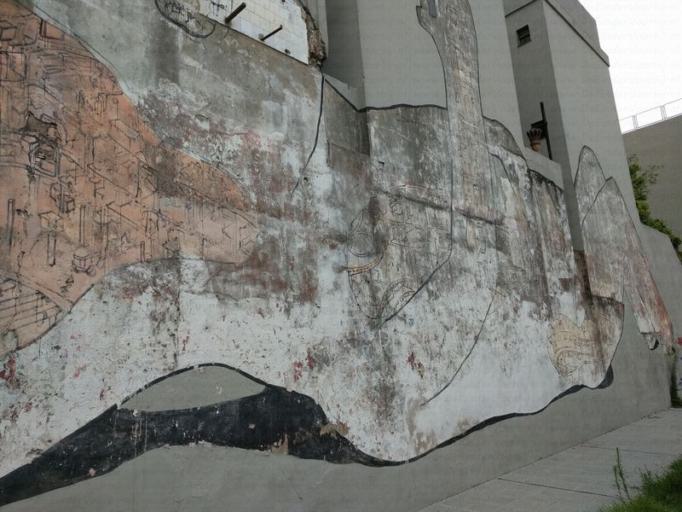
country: AR
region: Buenos Aires F.D.
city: Colegiales
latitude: -34.5669
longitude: -58.4791
